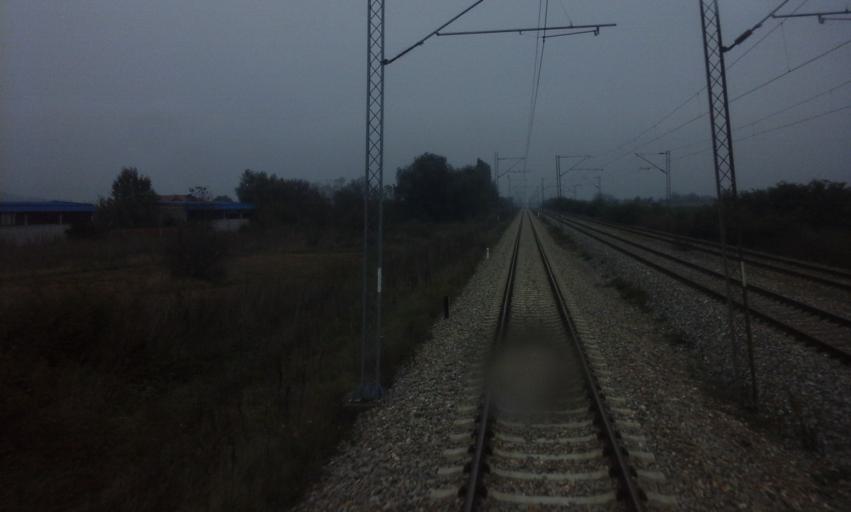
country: RS
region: Central Serbia
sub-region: Pomoravski Okrug
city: Paracin
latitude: 43.8825
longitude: 21.3859
